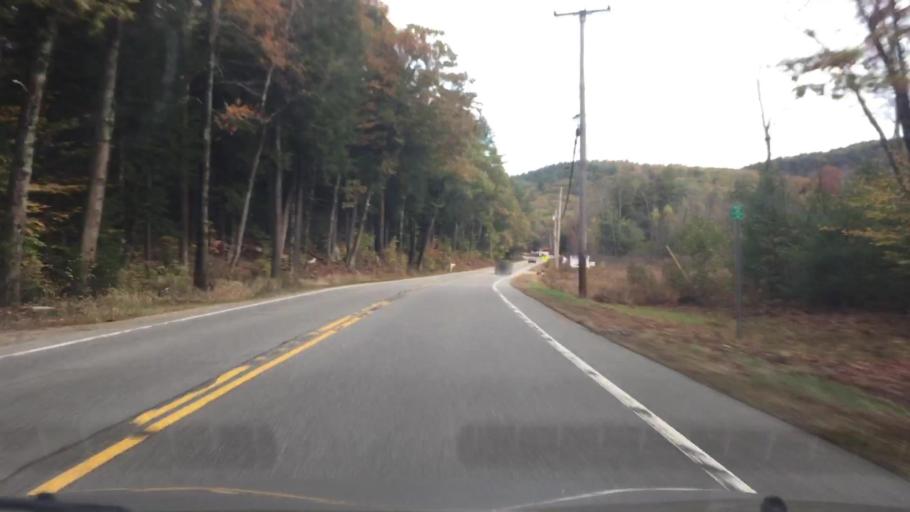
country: US
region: New Hampshire
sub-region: Cheshire County
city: Keene
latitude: 43.0124
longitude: -72.2627
